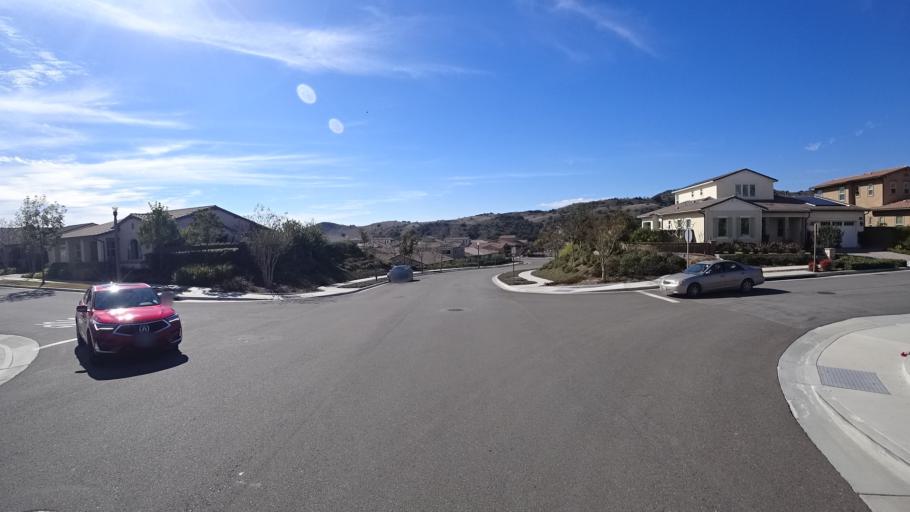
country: US
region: California
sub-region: Orange County
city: Ladera Ranch
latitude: 33.5364
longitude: -117.6060
